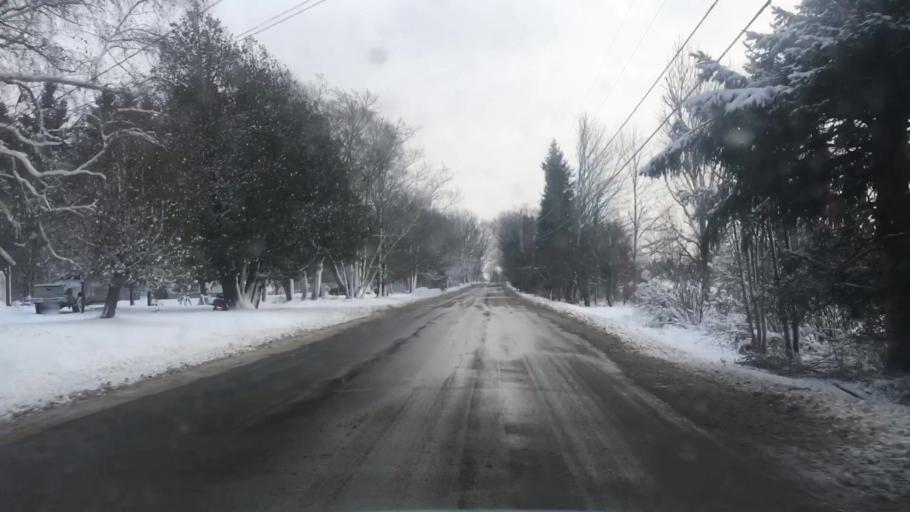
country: US
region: Maine
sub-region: Waldo County
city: Palermo
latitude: 44.3597
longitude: -69.4535
